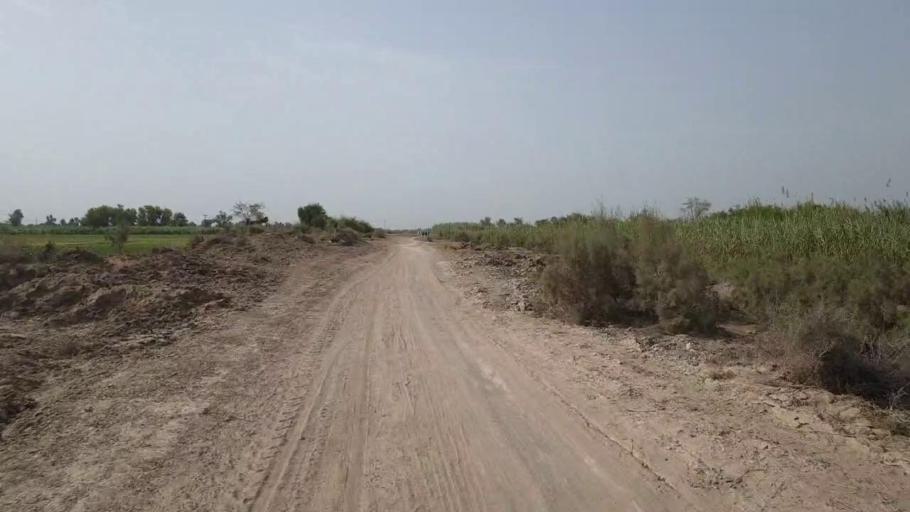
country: PK
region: Sindh
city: Daur
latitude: 26.4147
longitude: 68.1605
